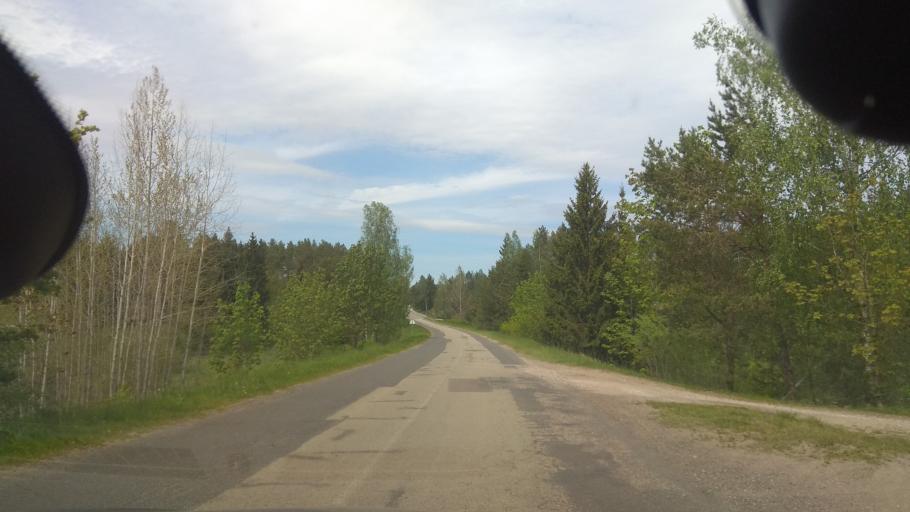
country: LT
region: Vilnius County
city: Ukmerge
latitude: 55.1371
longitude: 24.5943
